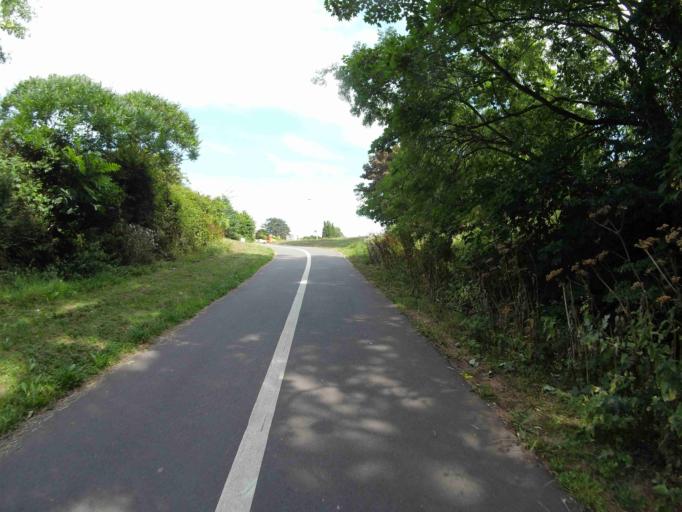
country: GB
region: England
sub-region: Devon
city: Exmouth
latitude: 50.6250
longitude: -3.3917
